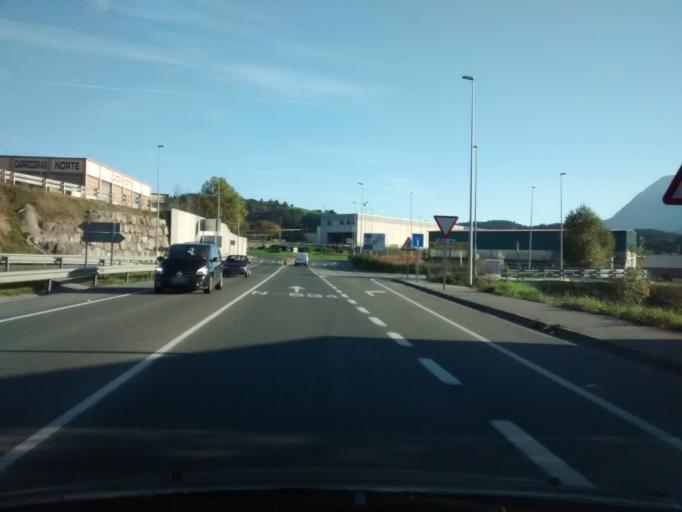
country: ES
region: Basque Country
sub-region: Bizkaia
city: Abadino
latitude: 43.1673
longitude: -2.6059
